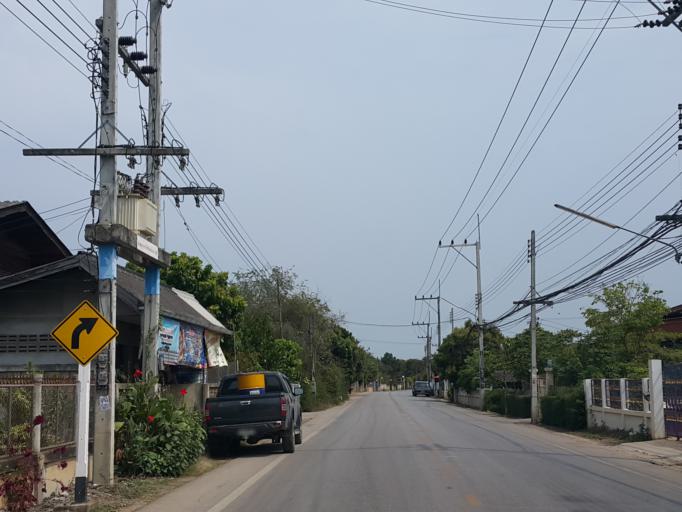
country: TH
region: Lampang
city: Ko Kha
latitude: 18.1619
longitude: 99.3811
